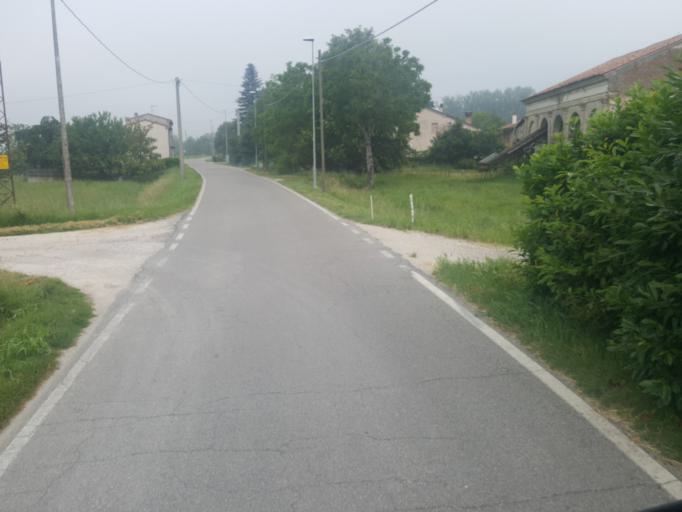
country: IT
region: Veneto
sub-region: Provincia di Rovigo
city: Canaro
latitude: 44.9339
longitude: 11.6578
